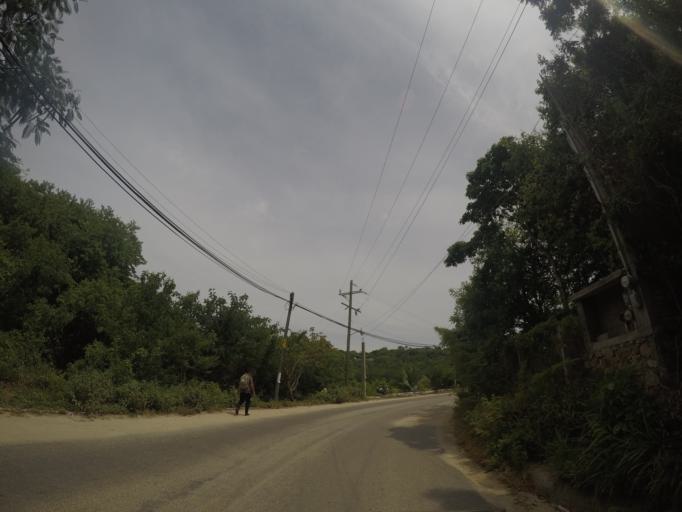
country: MX
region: Oaxaca
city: San Pedro Pochutla
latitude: 15.6663
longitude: -96.4996
